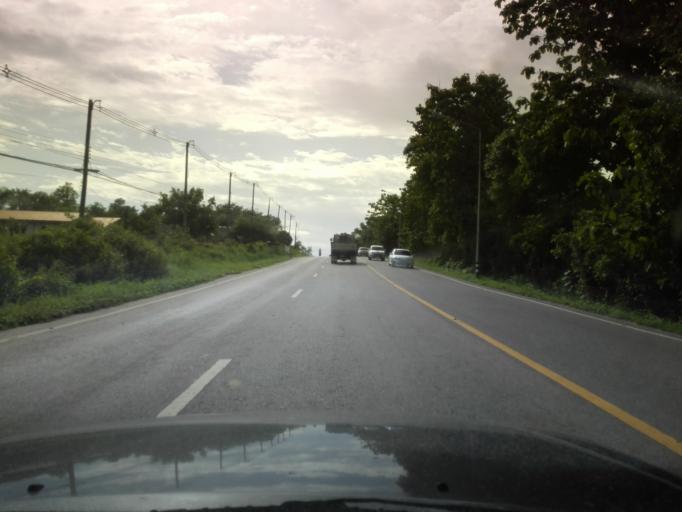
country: TH
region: Tak
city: Mae Ramat
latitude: 16.9702
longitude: 98.5384
